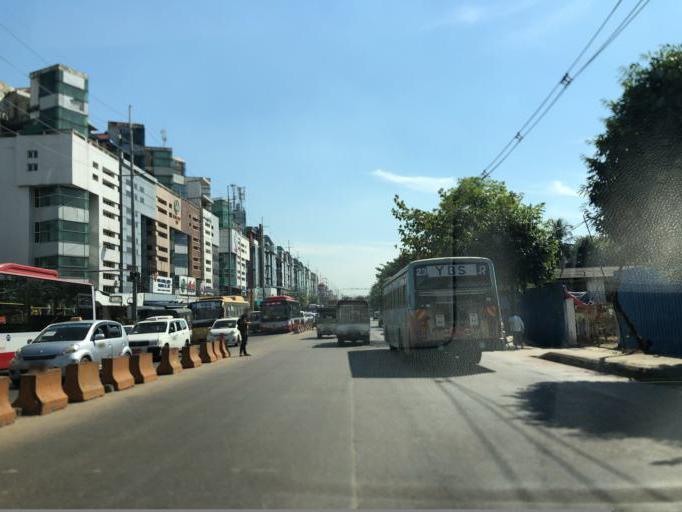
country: MM
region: Yangon
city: Yangon
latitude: 16.8325
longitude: 96.1209
